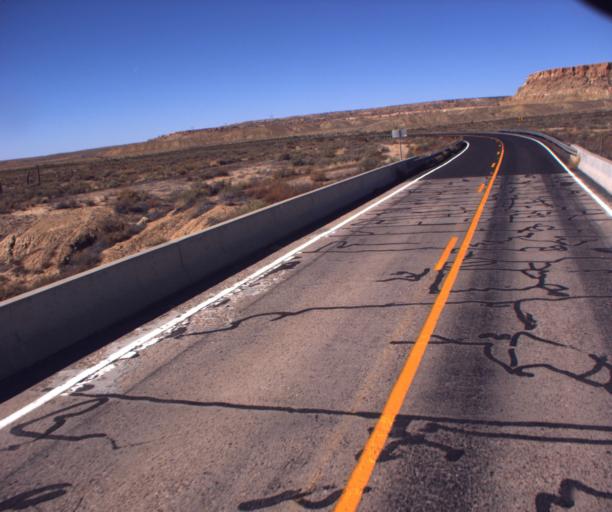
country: US
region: Arizona
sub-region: Navajo County
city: First Mesa
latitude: 35.9831
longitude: -110.7073
